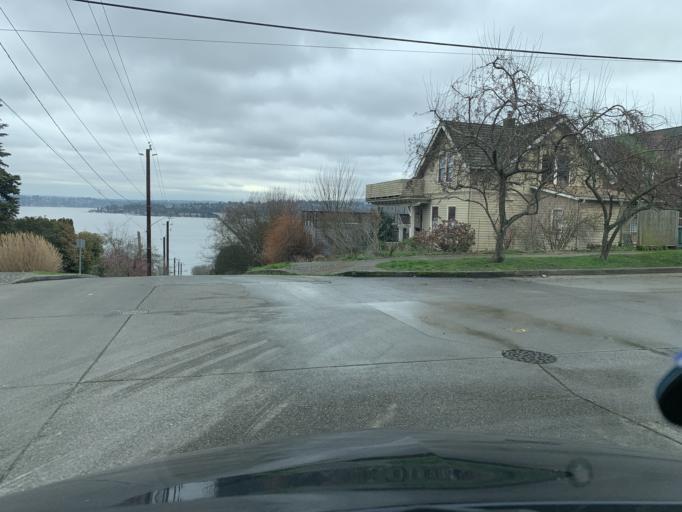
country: US
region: Washington
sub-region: King County
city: Seattle
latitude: 47.5913
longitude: -122.2908
